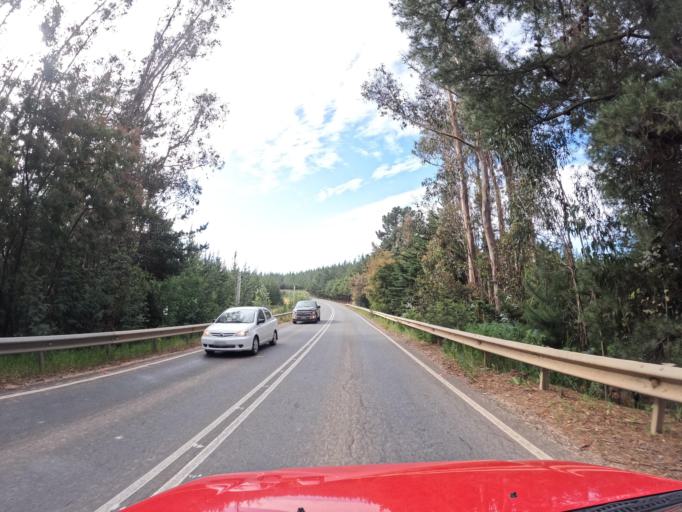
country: CL
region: O'Higgins
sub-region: Provincia de Colchagua
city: Santa Cruz
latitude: -34.3471
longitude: -71.8703
